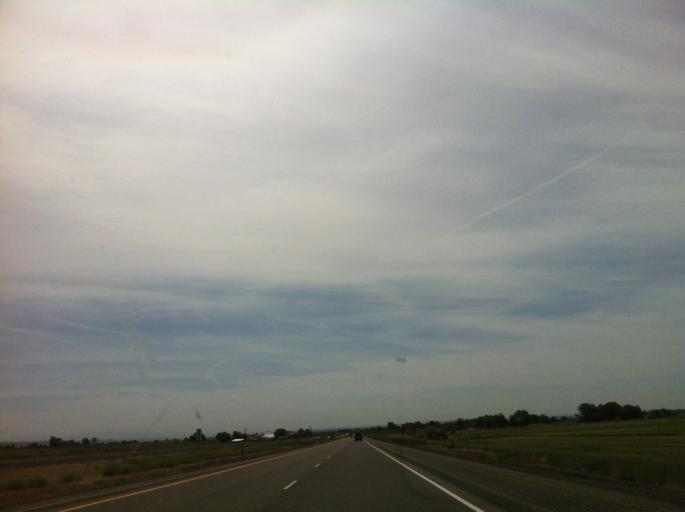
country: US
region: Oregon
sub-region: Malheur County
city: Ontario
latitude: 44.0898
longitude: -117.0260
